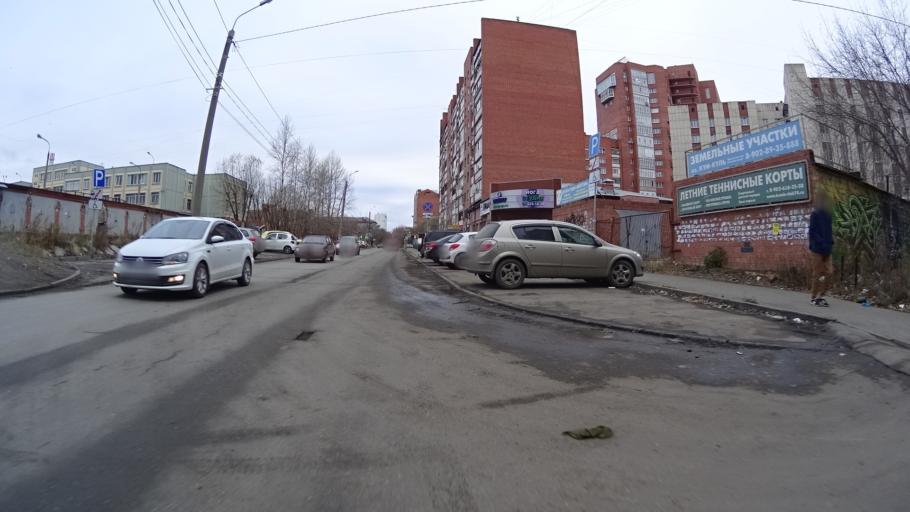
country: RU
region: Chelyabinsk
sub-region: Gorod Chelyabinsk
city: Chelyabinsk
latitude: 55.1537
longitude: 61.3781
